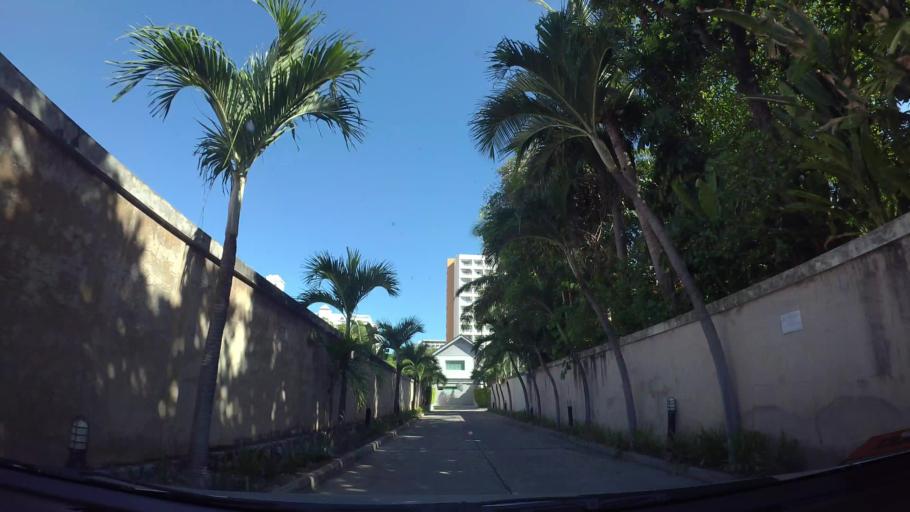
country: TH
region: Chon Buri
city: Phatthaya
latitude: 12.9070
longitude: 100.8728
